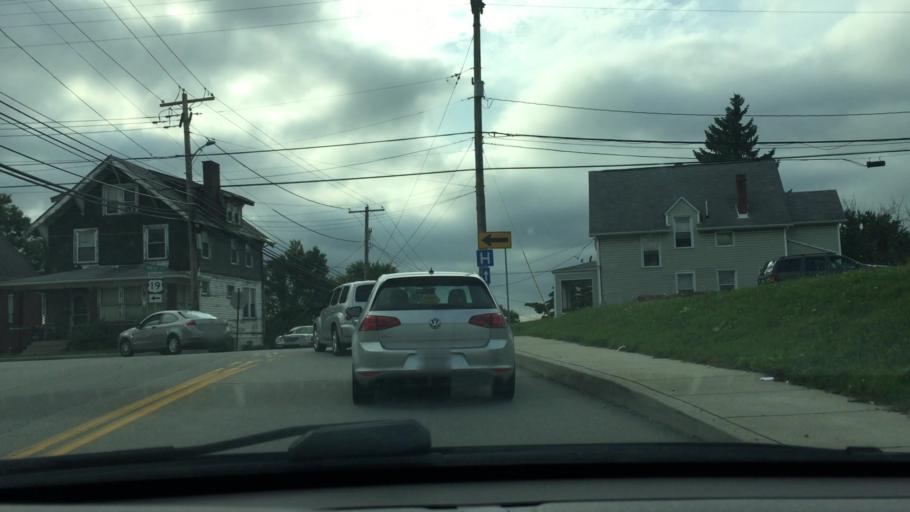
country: US
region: Pennsylvania
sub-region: Washington County
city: East Washington
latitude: 40.1802
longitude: -80.2404
